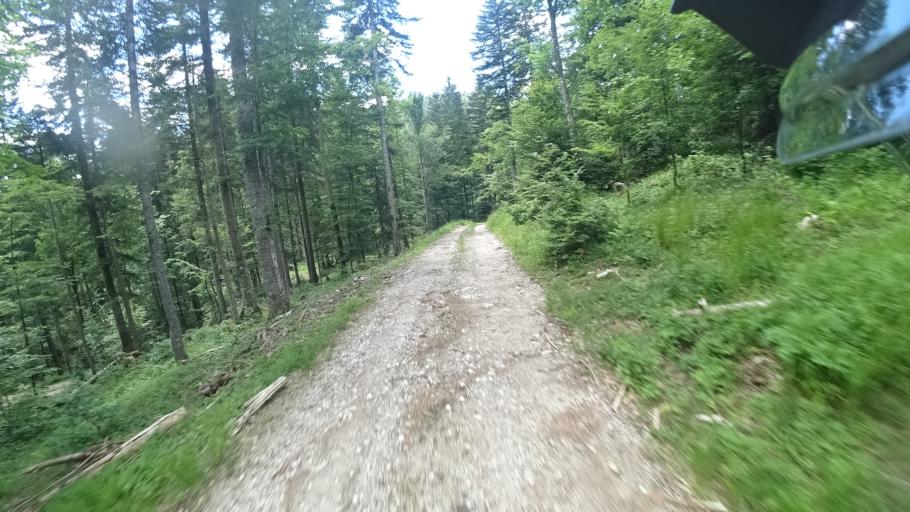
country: SI
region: Osilnica
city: Osilnica
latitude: 45.5144
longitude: 14.6155
